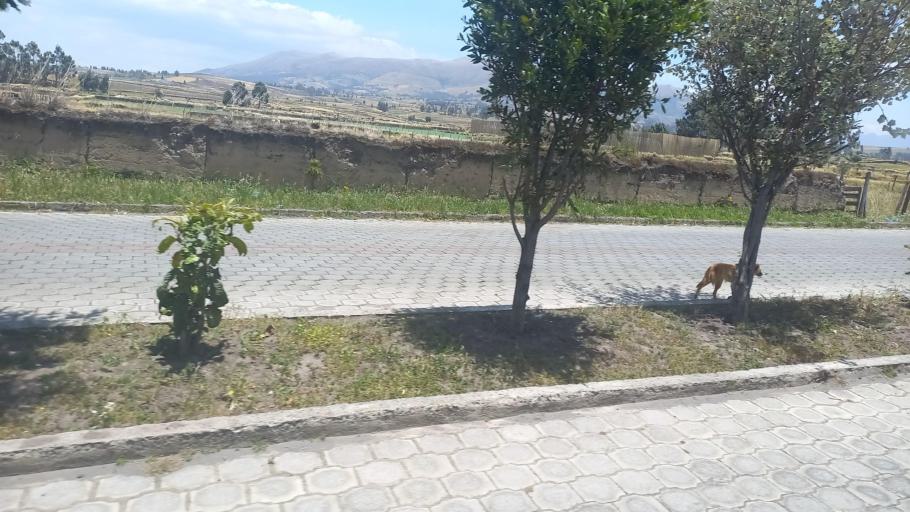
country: EC
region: Pichincha
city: Cayambe
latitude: 0.1450
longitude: -78.0708
